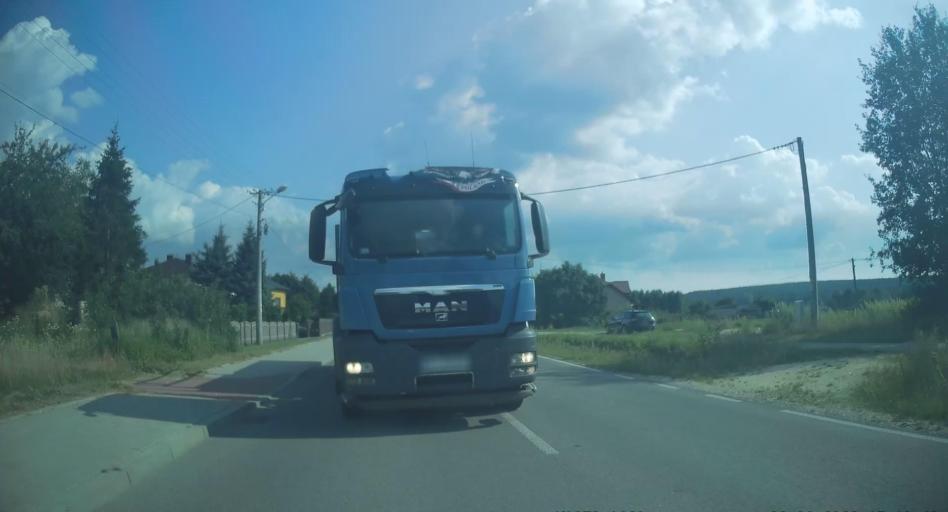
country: PL
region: Swietokrzyskie
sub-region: Powiat konecki
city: Radoszyce
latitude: 51.0532
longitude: 20.2803
